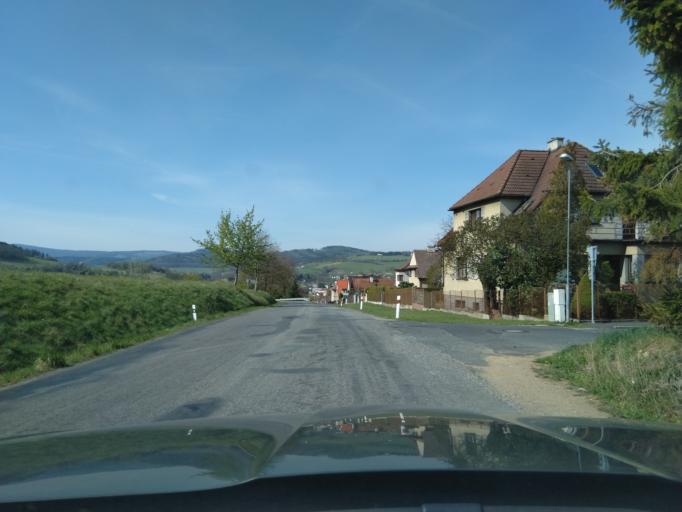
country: CZ
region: Plzensky
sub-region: Okres Klatovy
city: Susice
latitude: 49.2346
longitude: 13.5312
